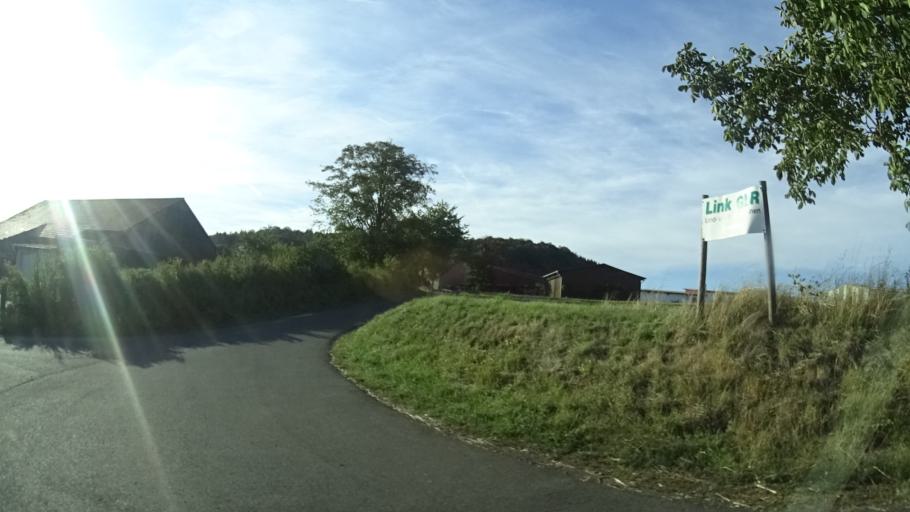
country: DE
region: Hesse
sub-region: Regierungsbezirk Giessen
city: Freiensteinau
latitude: 50.3979
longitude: 9.4478
